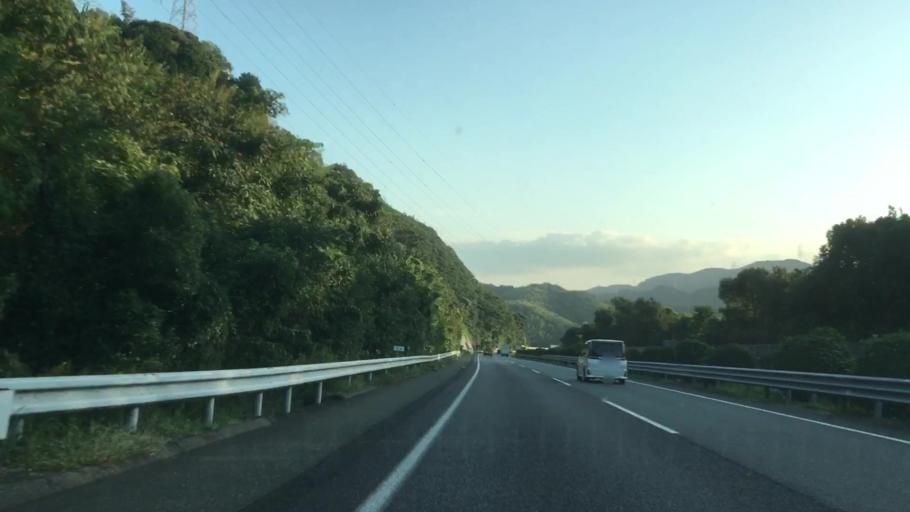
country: JP
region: Yamaguchi
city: Shimonoseki
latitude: 33.9138
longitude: 130.9760
